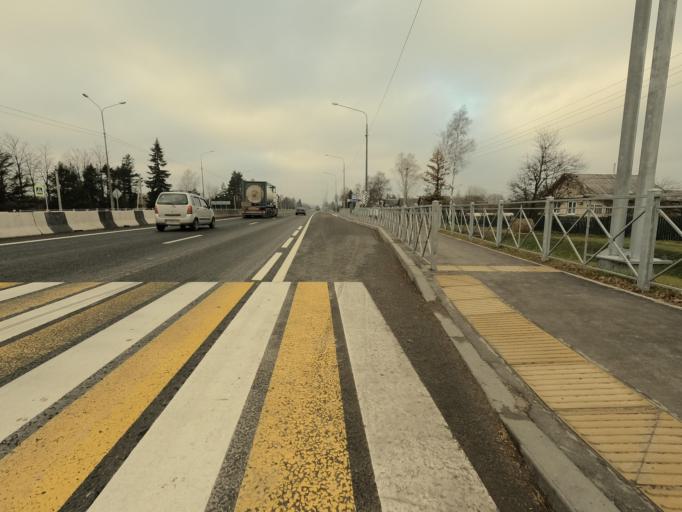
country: RU
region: Leningrad
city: Mga
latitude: 59.7171
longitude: 31.1094
